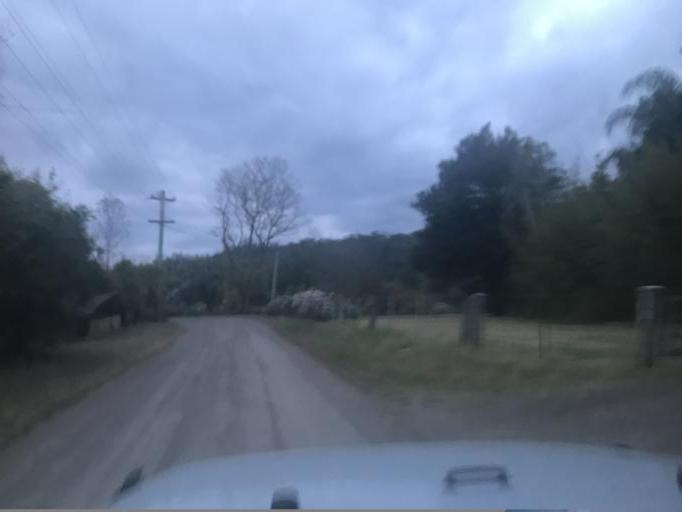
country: AU
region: New South Wales
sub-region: Hawkesbury
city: Pitt Town
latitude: -33.4866
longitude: 150.8925
